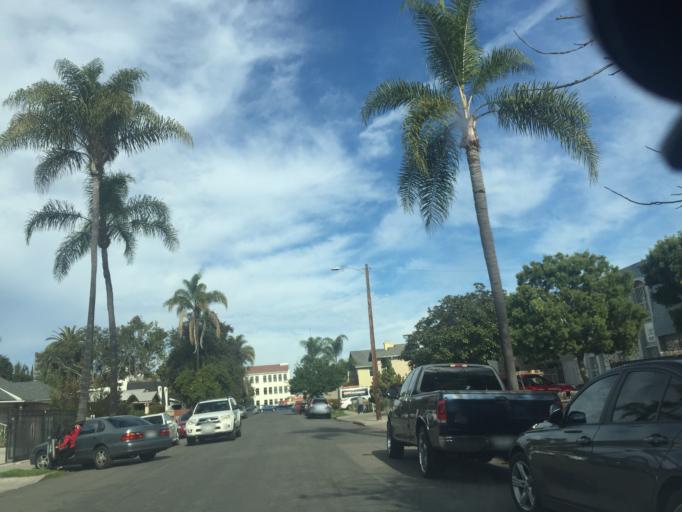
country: US
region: California
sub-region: San Diego County
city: Lemon Grove
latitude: 32.7539
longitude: -117.0976
